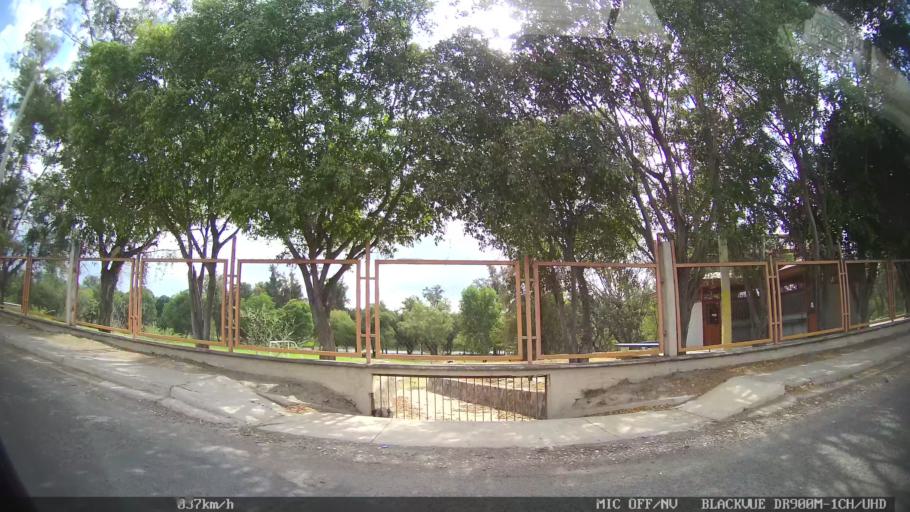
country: MX
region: Jalisco
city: Tlaquepaque
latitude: 20.6649
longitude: -103.2673
